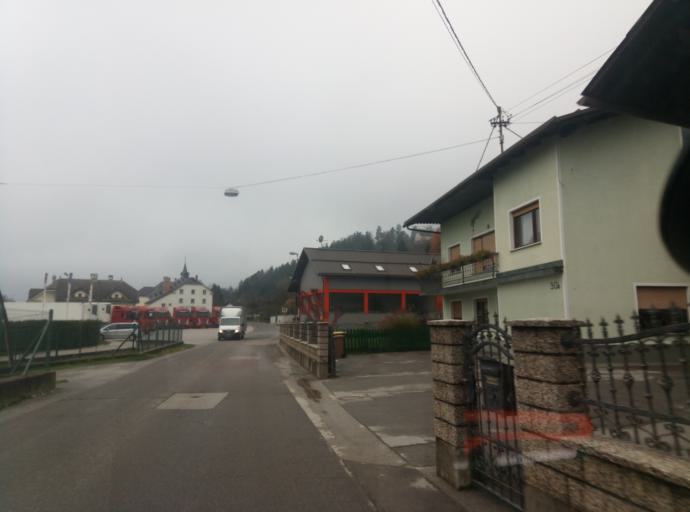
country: SI
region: Vodice
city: Vodice
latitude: 46.1730
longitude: 14.4828
